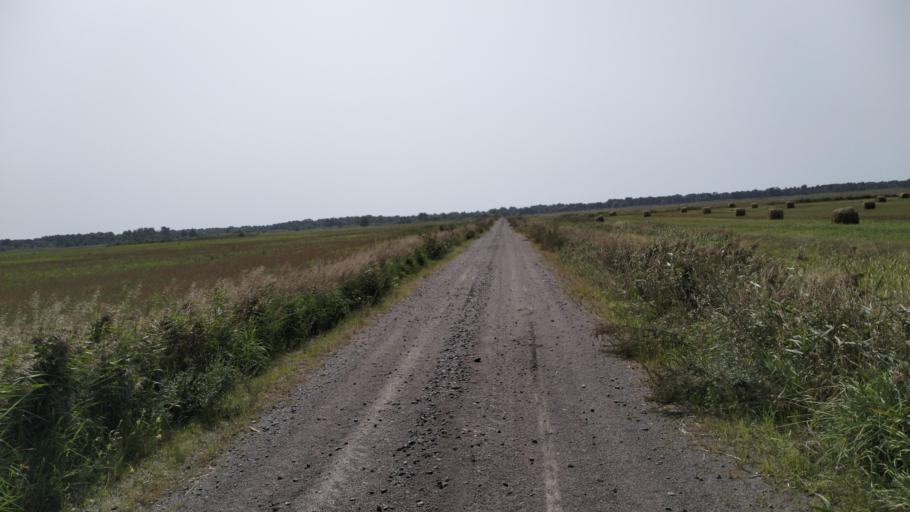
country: BY
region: Brest
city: Davyd-Haradok
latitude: 51.9788
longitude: 27.1745
